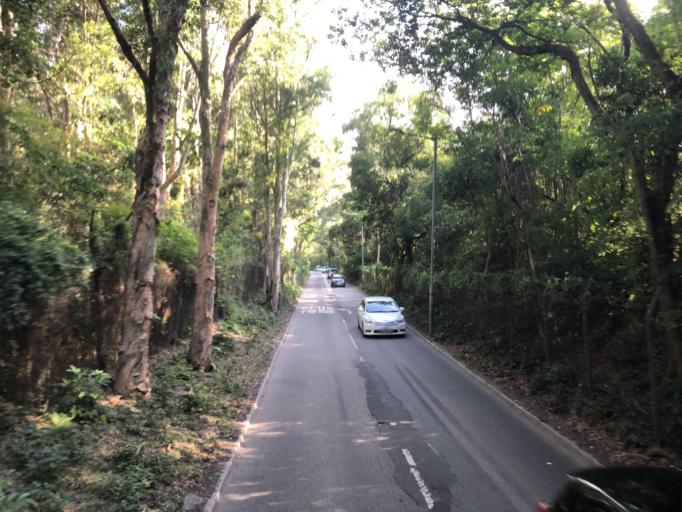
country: HK
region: Tai Po
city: Tai Po
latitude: 22.4900
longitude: 114.1170
